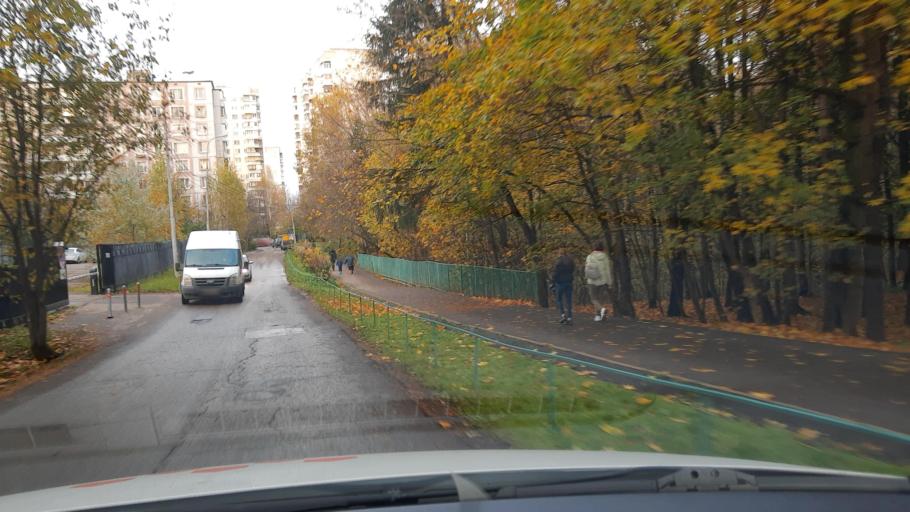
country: RU
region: Moscow
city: Yasenevo
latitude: 55.6030
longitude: 37.5546
